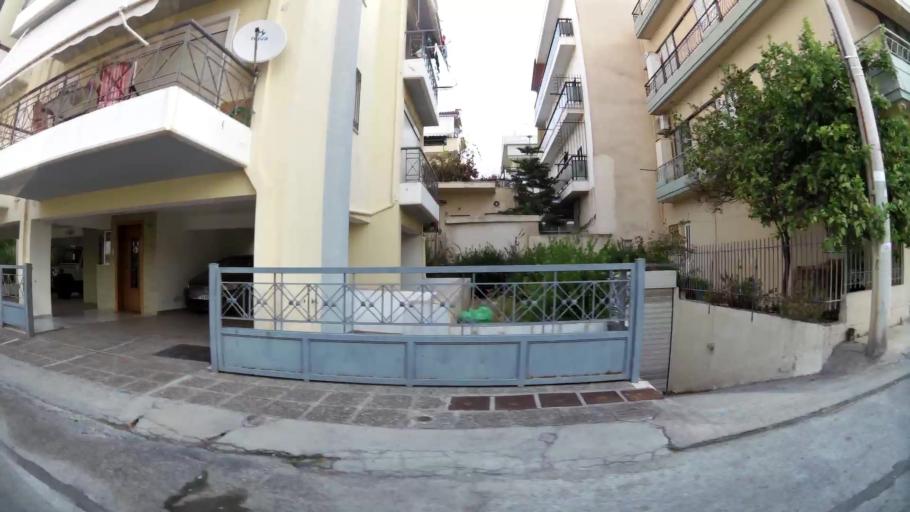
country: GR
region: Attica
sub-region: Nomarchia Athinas
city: Agios Dimitrios
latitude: 37.9372
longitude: 23.7243
